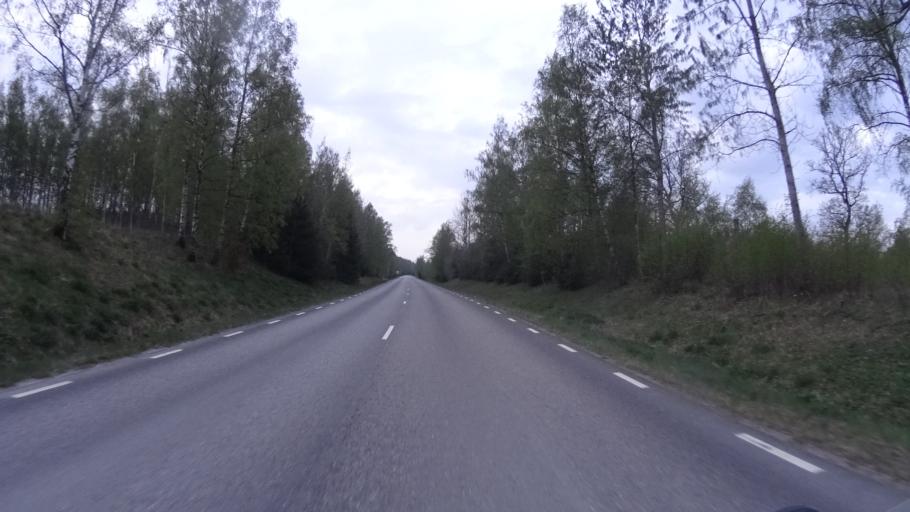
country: SE
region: Vaestra Goetaland
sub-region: Gotene Kommun
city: Goetene
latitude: 58.6172
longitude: 13.4029
